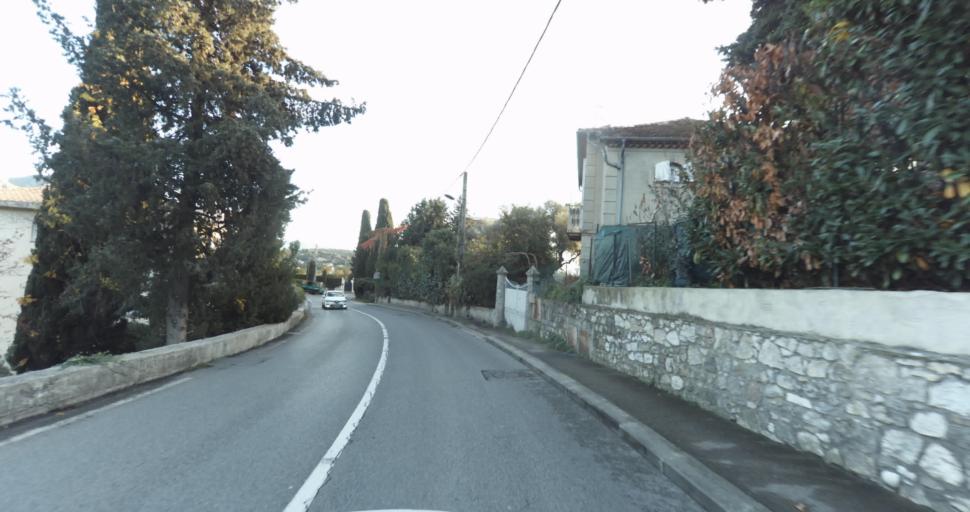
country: FR
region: Provence-Alpes-Cote d'Azur
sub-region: Departement des Alpes-Maritimes
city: Vence
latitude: 43.7216
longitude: 7.1204
